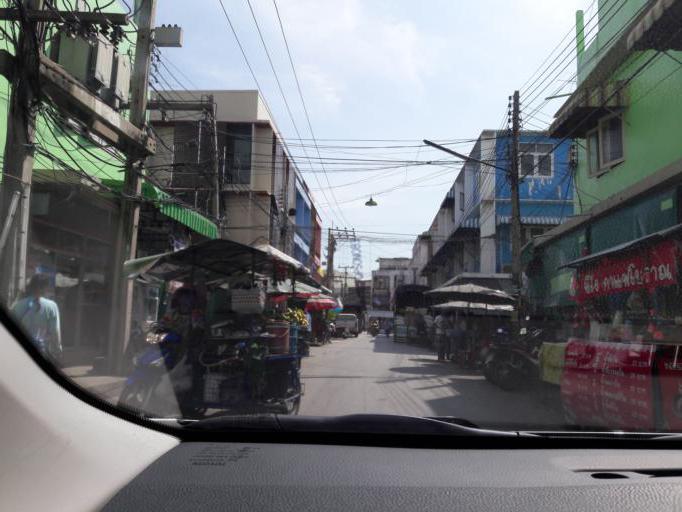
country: TH
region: Ang Thong
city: Ang Thong
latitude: 14.5922
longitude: 100.4500
